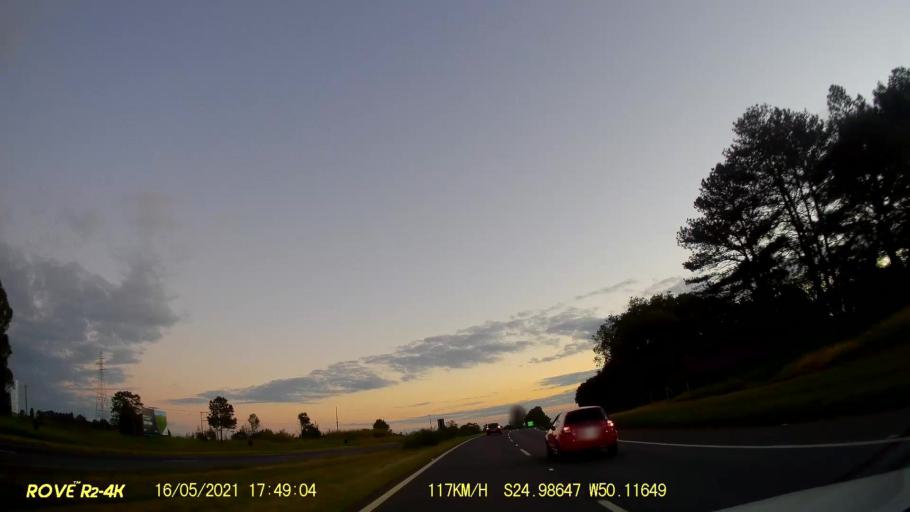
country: BR
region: Parana
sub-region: Carambei
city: Carambei
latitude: -24.9861
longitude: -50.1169
